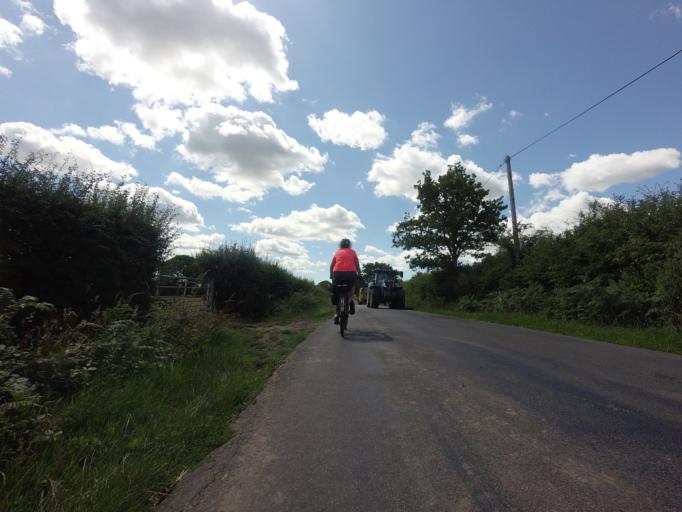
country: GB
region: England
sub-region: East Sussex
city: Hailsham
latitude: 50.8840
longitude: 0.1862
